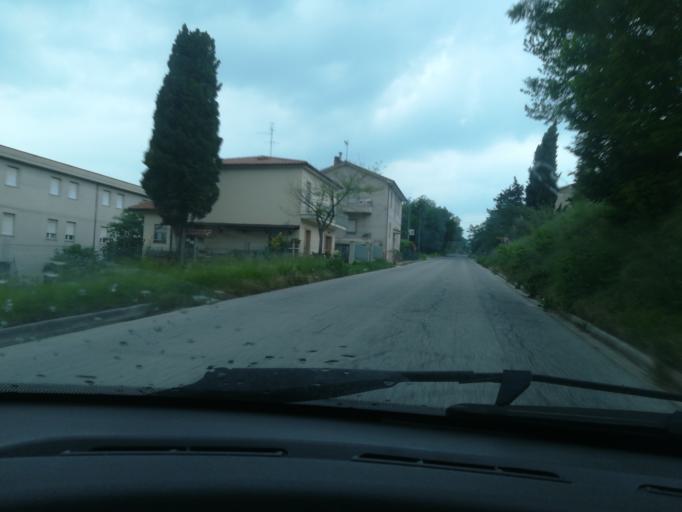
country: IT
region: The Marches
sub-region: Provincia di Macerata
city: Treia
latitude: 43.3007
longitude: 13.3153
